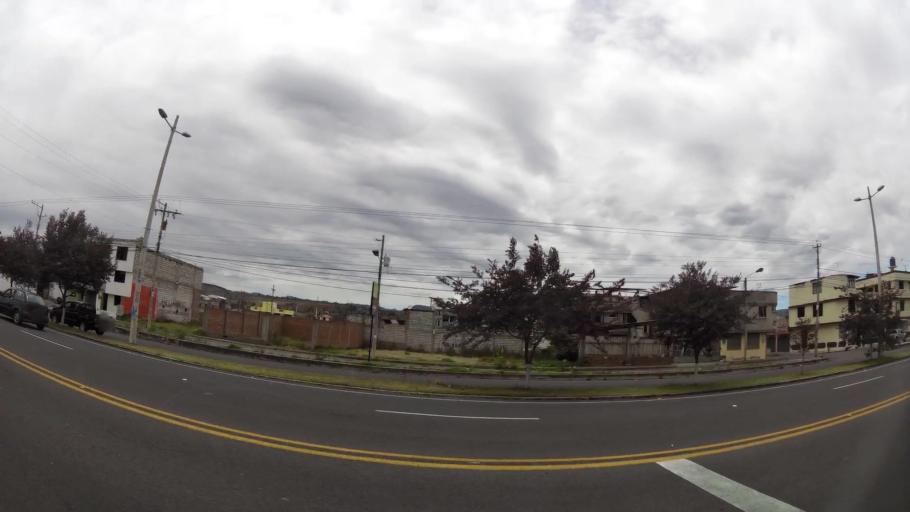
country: EC
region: Cotopaxi
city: Latacunga
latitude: -0.9668
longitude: -78.6103
